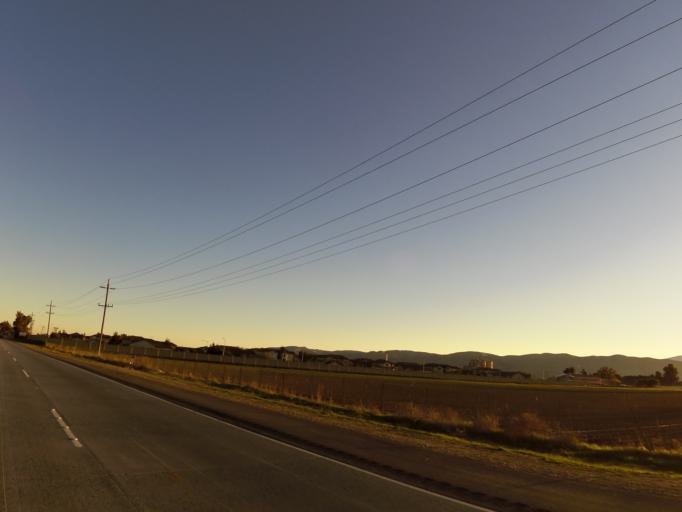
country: US
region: California
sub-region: Monterey County
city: Greenfield
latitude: 36.3346
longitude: -121.2502
